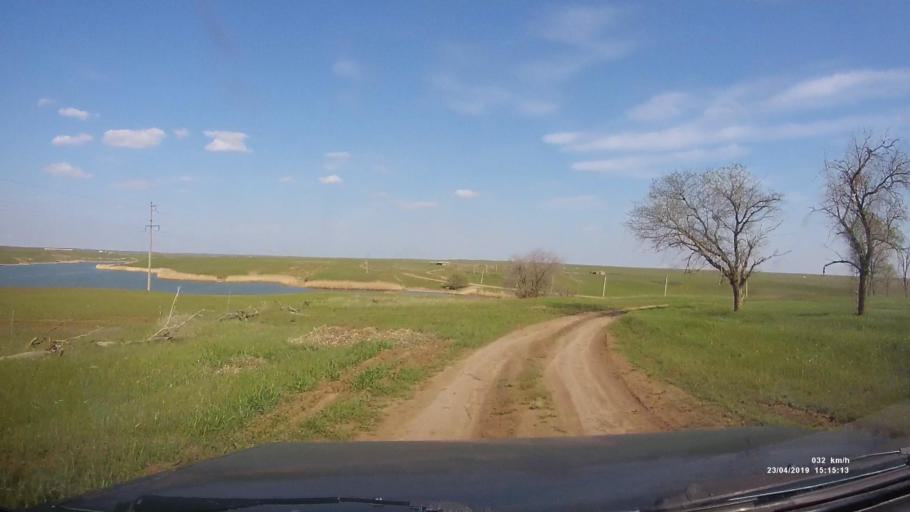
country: RU
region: Rostov
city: Remontnoye
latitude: 46.5396
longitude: 42.9688
